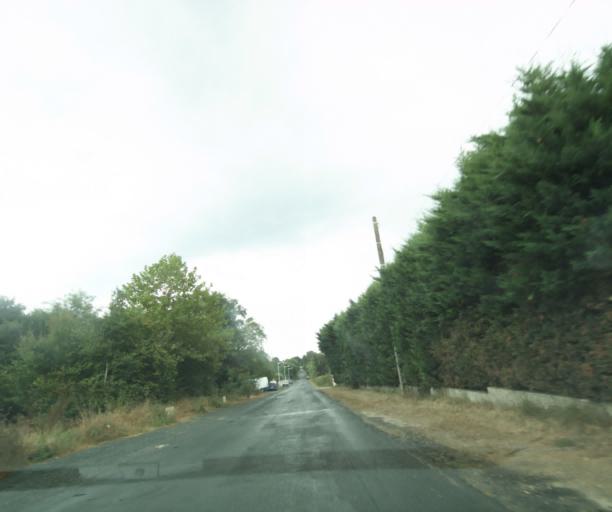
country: FR
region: Poitou-Charentes
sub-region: Departement de la Charente-Maritime
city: Tonnay-Charente
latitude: 45.9431
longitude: -0.8802
